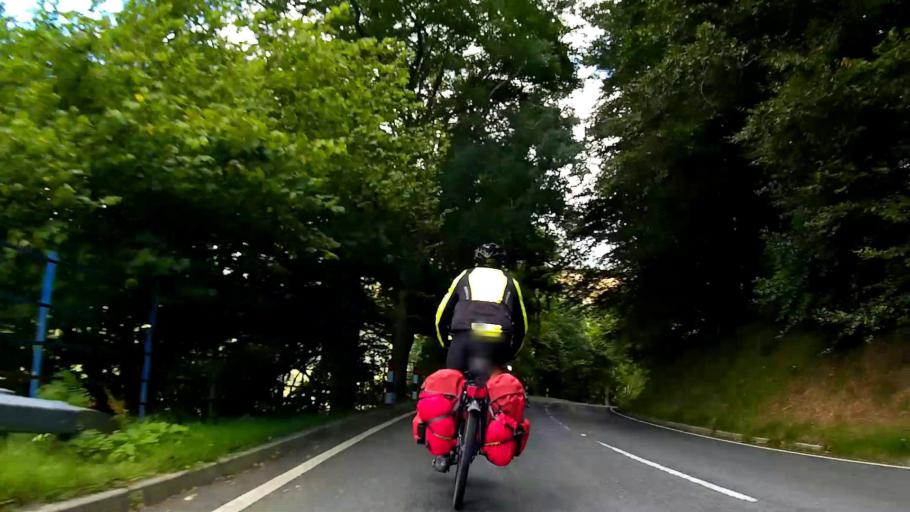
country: GB
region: Wales
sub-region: Denbighshire
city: Llangollen
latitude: 53.0071
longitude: -3.1941
